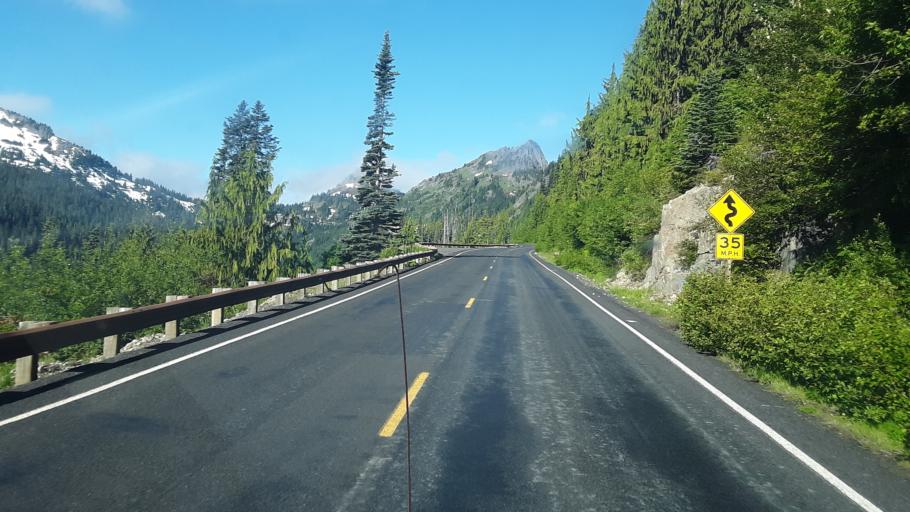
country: US
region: Washington
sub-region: King County
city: Enumclaw
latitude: 46.8908
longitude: -121.4911
